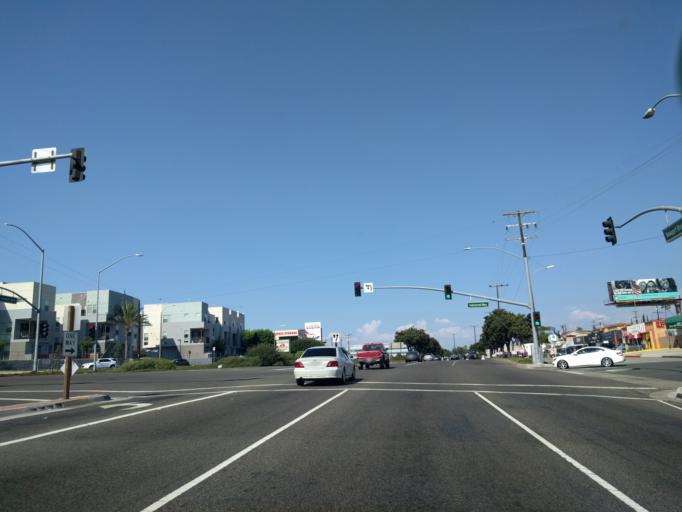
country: US
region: California
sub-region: Orange County
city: Costa Mesa
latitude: 33.6308
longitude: -117.9252
